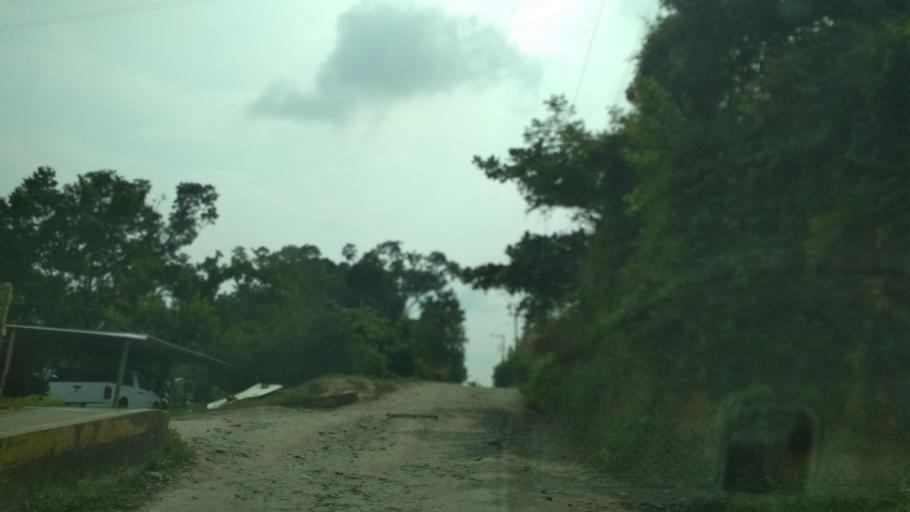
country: MM
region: Kayah
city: Loikaw
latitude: 20.2164
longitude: 97.2849
